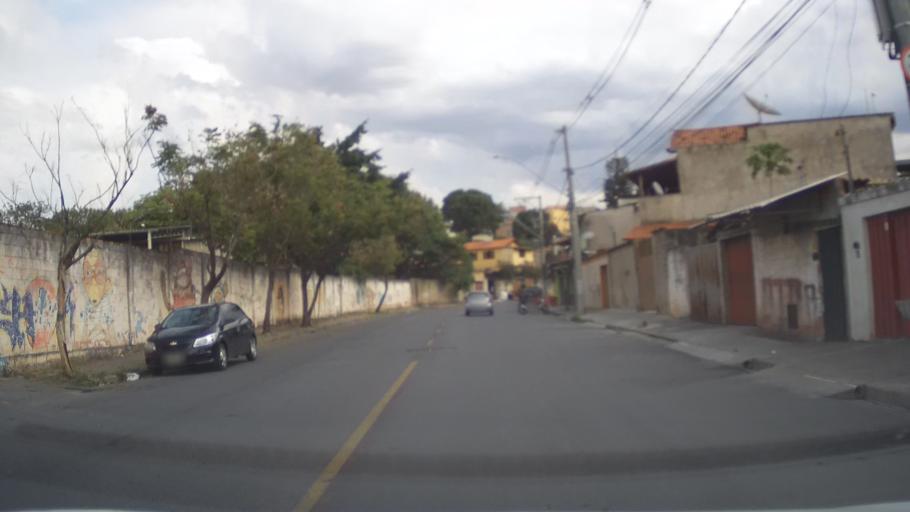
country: BR
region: Minas Gerais
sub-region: Belo Horizonte
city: Belo Horizonte
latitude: -19.8587
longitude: -43.8974
